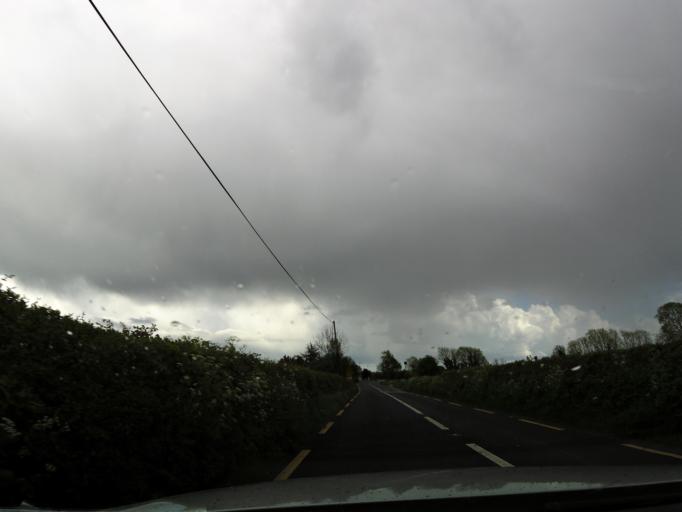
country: IE
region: Munster
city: Thurles
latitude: 52.6945
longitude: -7.8138
